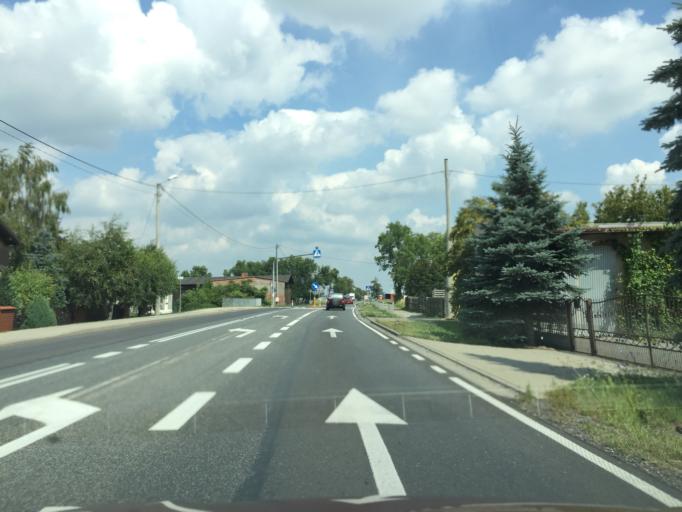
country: PL
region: Greater Poland Voivodeship
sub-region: Powiat kaliski
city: Stawiszyn
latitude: 51.8963
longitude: 18.1022
